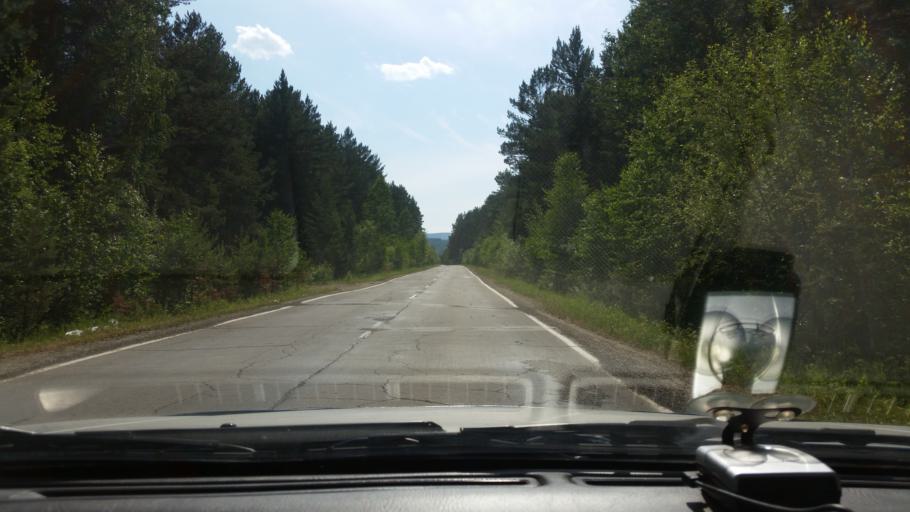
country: RU
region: Irkutsk
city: Baklashi
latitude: 52.2082
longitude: 103.9634
